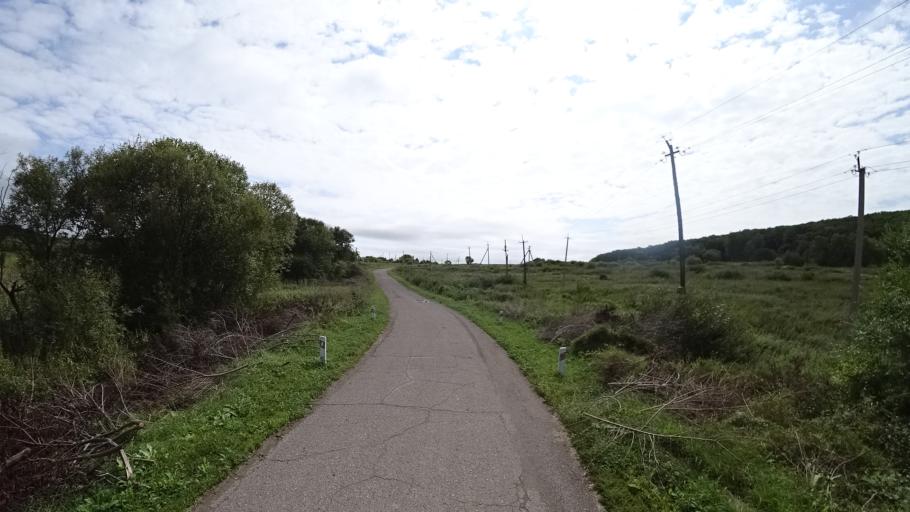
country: RU
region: Primorskiy
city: Lyalichi
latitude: 44.1360
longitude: 132.3875
